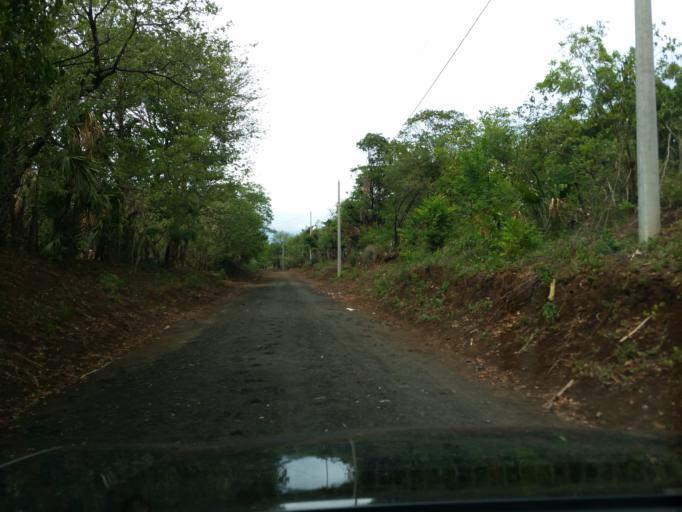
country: NI
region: Managua
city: Carlos Fonseca Amador
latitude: 11.9679
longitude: -86.4211
